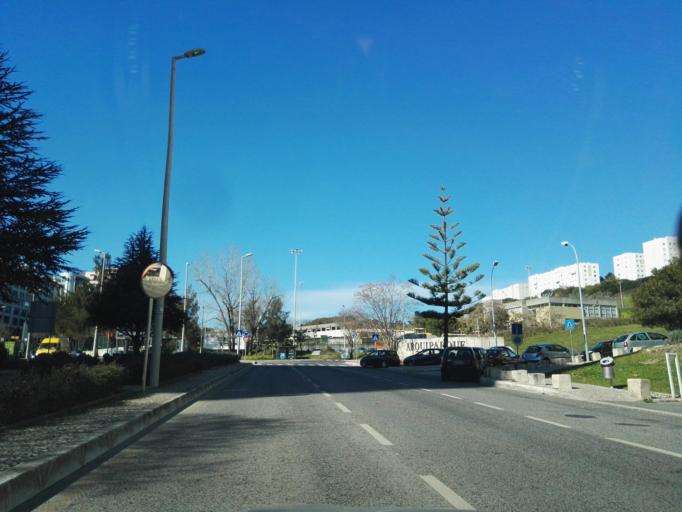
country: PT
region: Lisbon
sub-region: Oeiras
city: Alges
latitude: 38.7147
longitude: -9.2282
